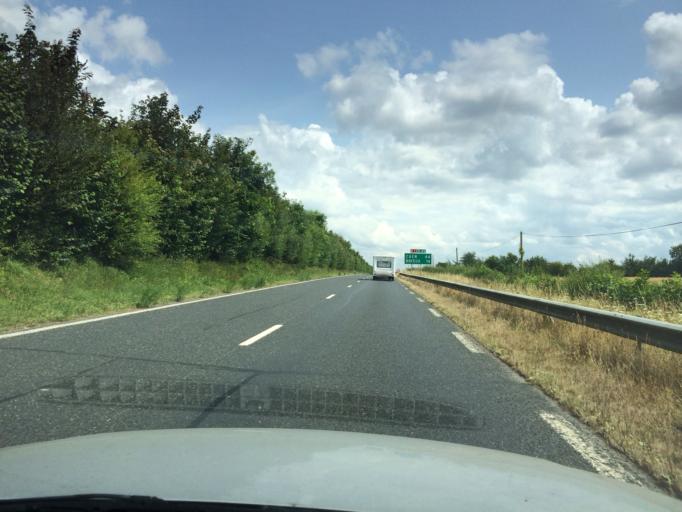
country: FR
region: Lower Normandy
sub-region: Departement du Calvados
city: Grandcamp-Maisy
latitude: 49.3387
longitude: -0.9387
